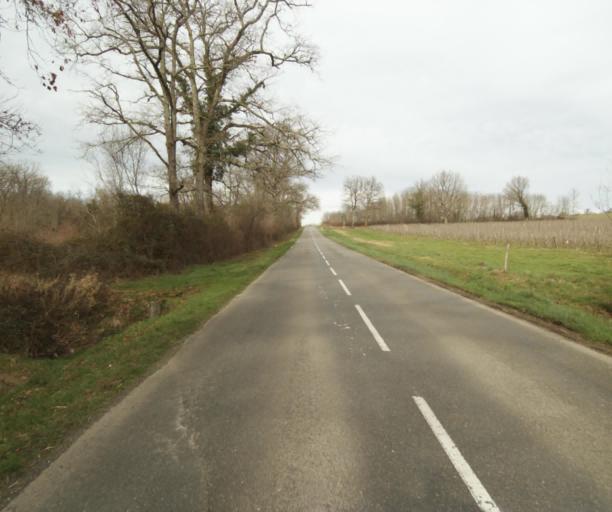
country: FR
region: Aquitaine
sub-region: Departement des Landes
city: Gabarret
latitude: 43.9568
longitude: 0.0078
